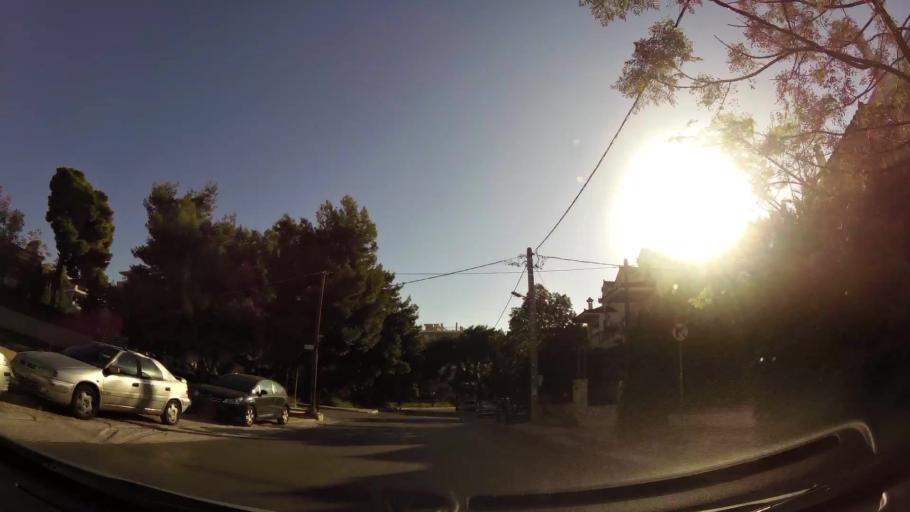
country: GR
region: Attica
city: Pefki
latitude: 38.0507
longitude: 23.7885
